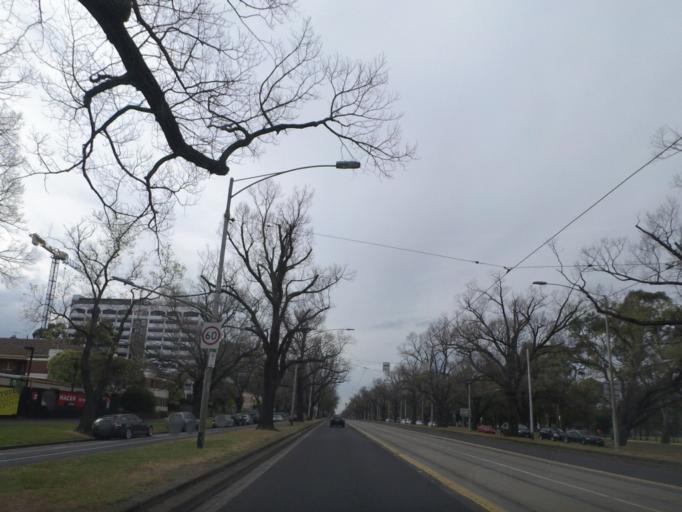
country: AU
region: Victoria
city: Carlton North
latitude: -37.7874
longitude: 144.9590
